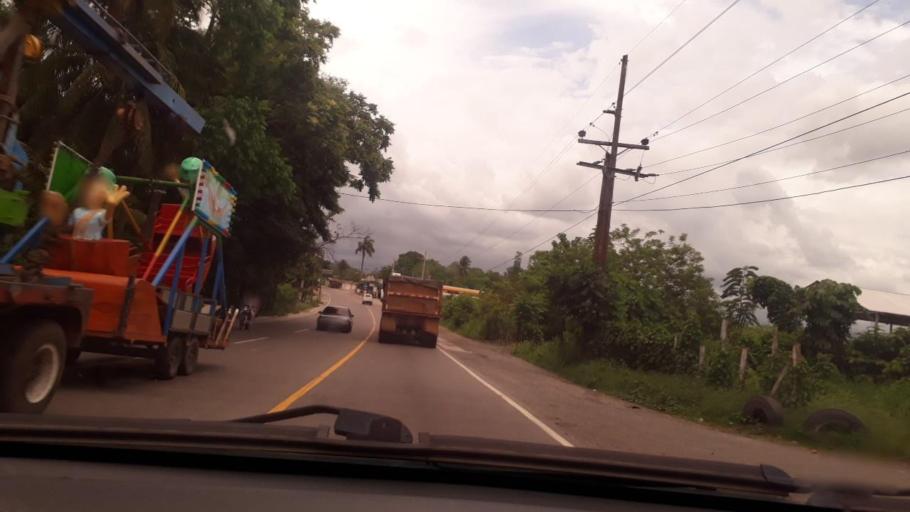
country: GT
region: Izabal
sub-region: Municipio de Los Amates
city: Los Amates
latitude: 15.2529
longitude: -89.1071
